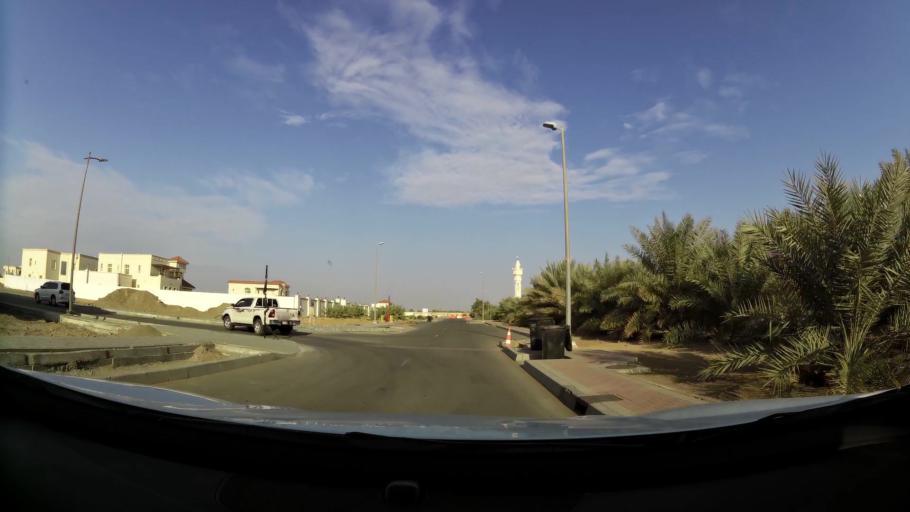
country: AE
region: Abu Dhabi
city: Al Ain
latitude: 24.0858
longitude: 55.8483
